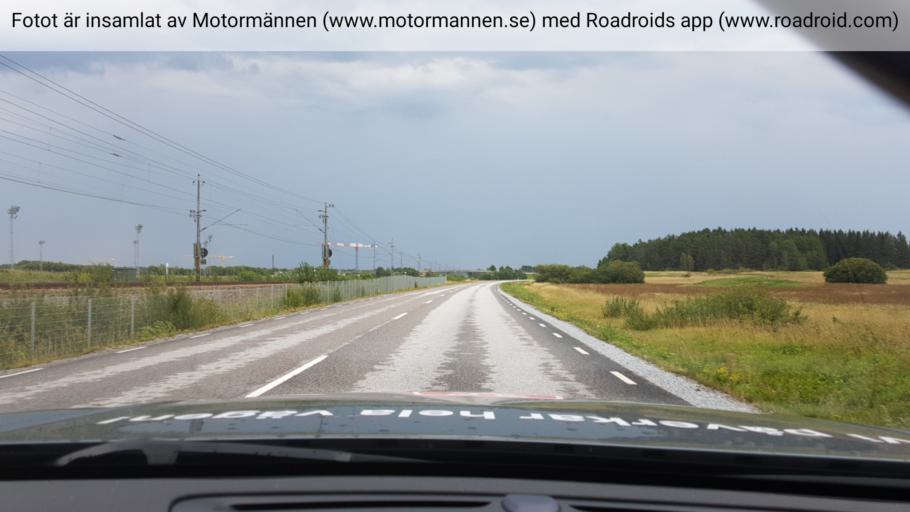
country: SE
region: Stockholm
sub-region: Upplands-Bro Kommun
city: Bro
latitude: 59.5203
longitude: 17.6056
